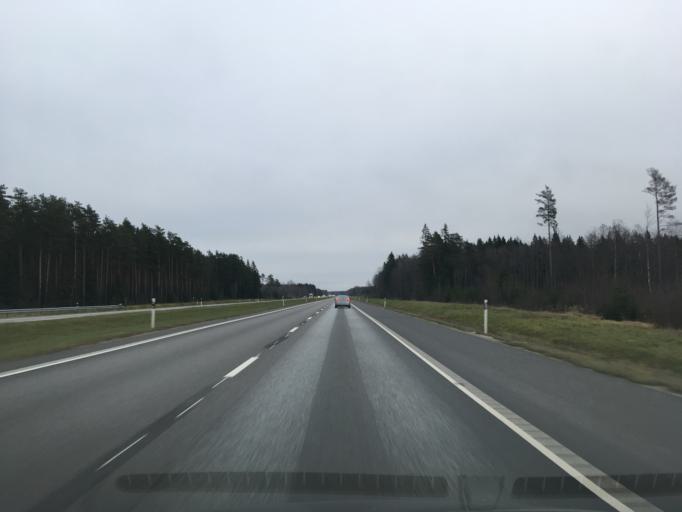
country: EE
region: Harju
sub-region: Loksa linn
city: Loksa
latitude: 59.4557
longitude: 25.8847
